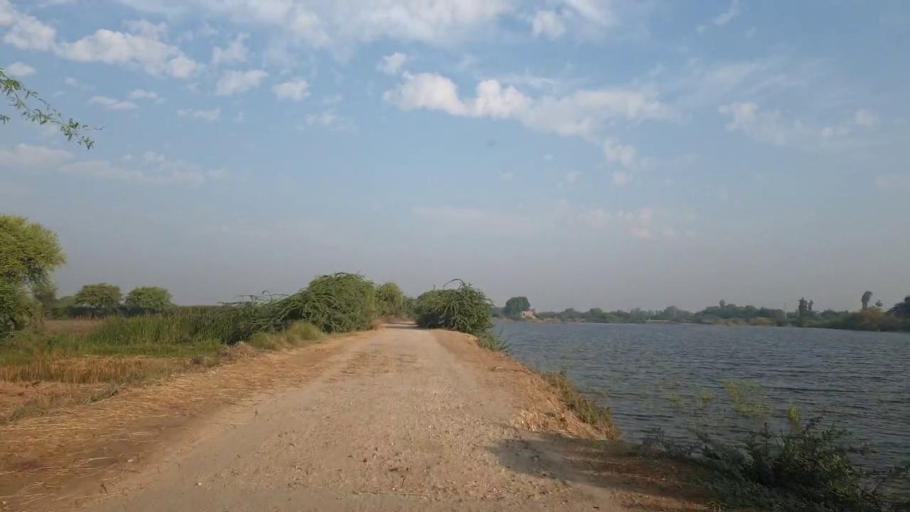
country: PK
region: Sindh
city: Tando Bago
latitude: 24.8010
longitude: 68.9597
